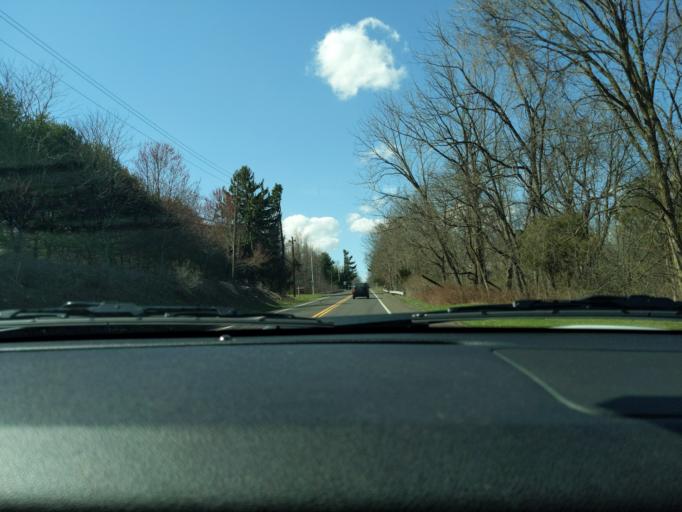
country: US
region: Pennsylvania
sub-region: Bucks County
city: Perkasie
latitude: 40.4180
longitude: -75.2733
